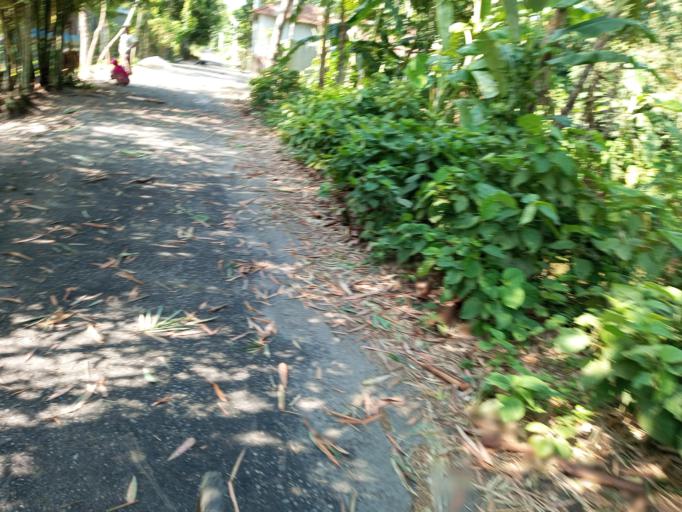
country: BD
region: Rangpur Division
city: Lalmanirhat
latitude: 25.9640
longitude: 89.2669
